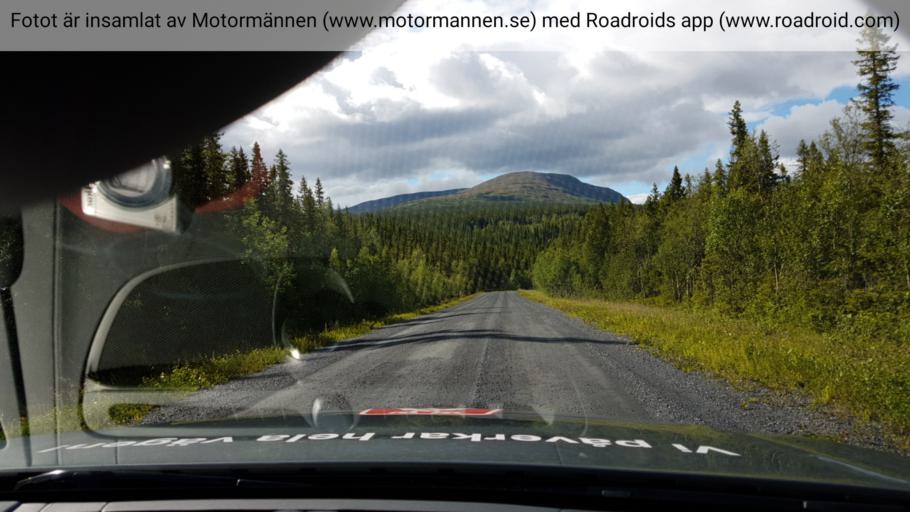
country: SE
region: Jaemtland
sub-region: Krokoms Kommun
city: Valla
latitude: 63.1039
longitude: 13.8700
